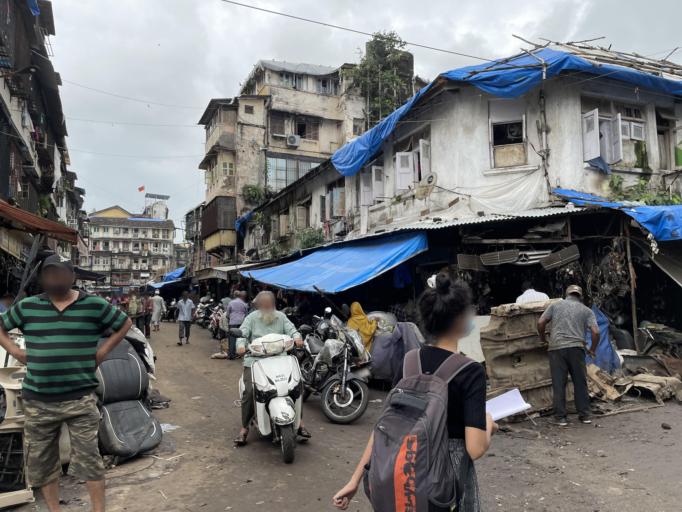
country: IN
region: Maharashtra
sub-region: Mumbai Suburban
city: Mumbai
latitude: 18.9608
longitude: 72.8294
